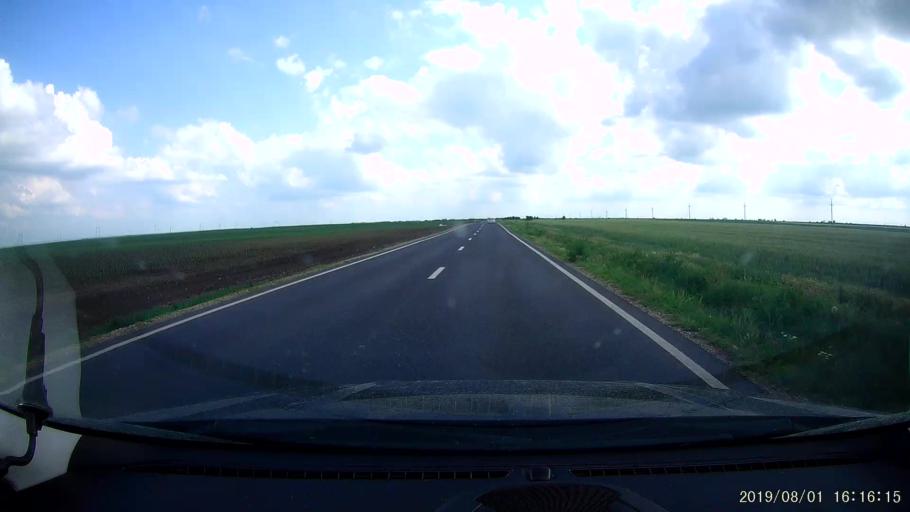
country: RO
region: Calarasi
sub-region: Comuna Stefan Voda
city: Stefan Voda
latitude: 44.3236
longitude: 27.3586
